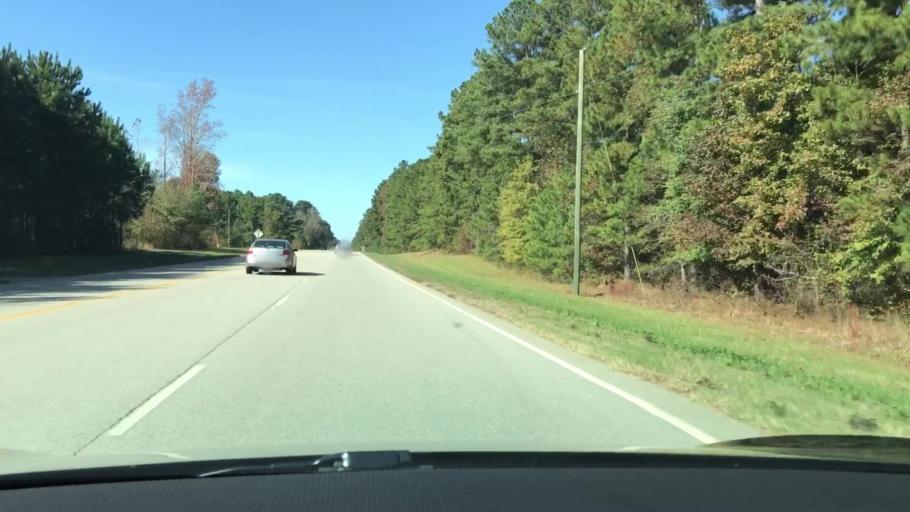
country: US
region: Georgia
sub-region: Warren County
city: Firing Range
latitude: 33.4790
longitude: -82.7391
